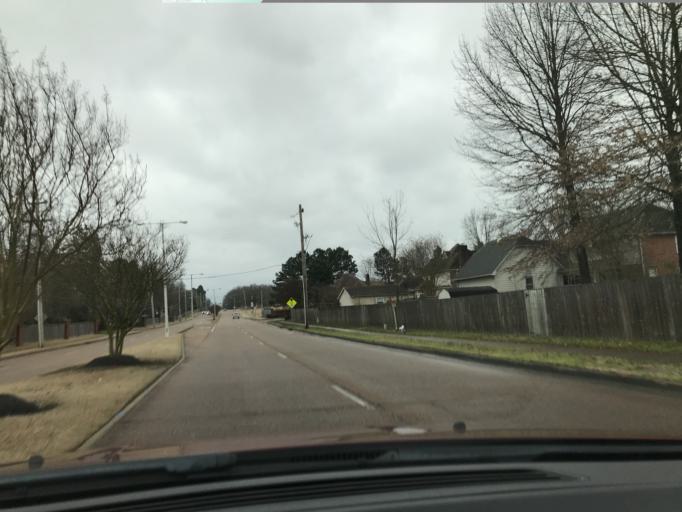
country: US
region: Tennessee
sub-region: Shelby County
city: Collierville
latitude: 35.0737
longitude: -89.6855
